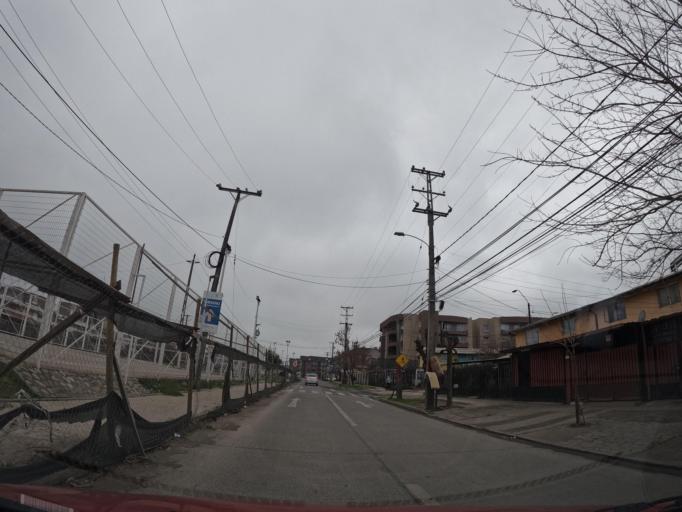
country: CL
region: Maule
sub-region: Provincia de Talca
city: Talca
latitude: -35.4376
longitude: -71.6309
